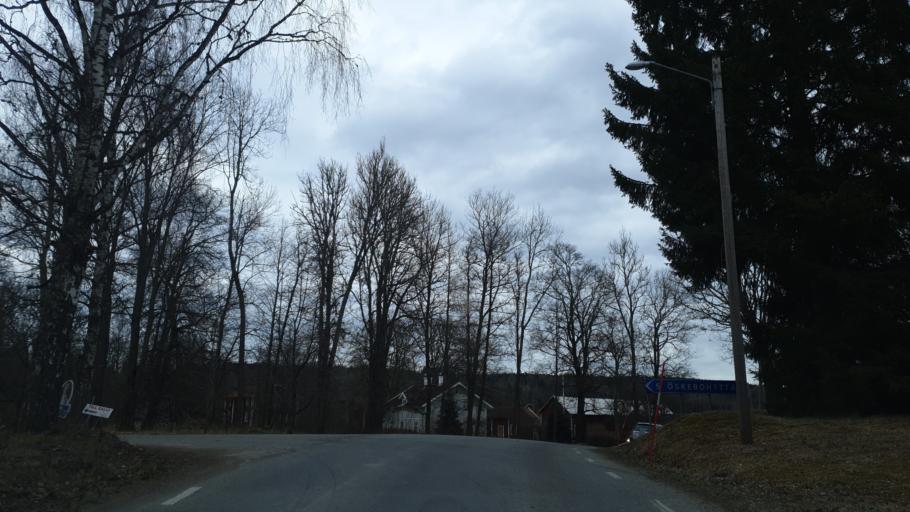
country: SE
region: OErebro
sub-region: Nora Kommun
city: As
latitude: 59.6108
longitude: 15.0066
